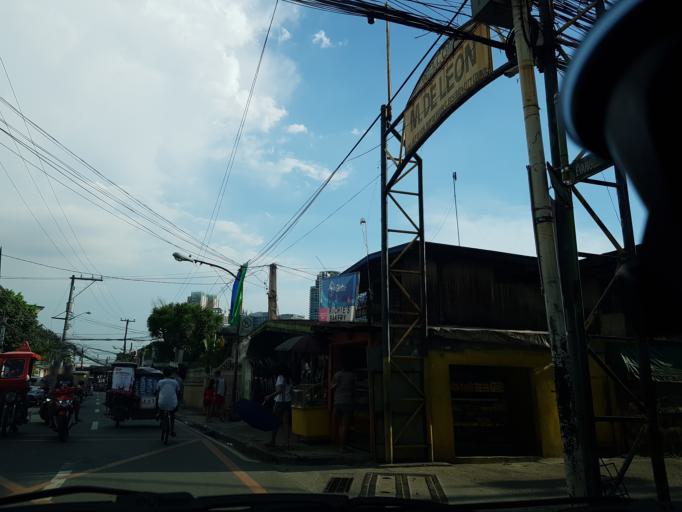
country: PH
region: Metro Manila
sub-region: Marikina
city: Calumpang
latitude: 14.6164
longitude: 121.0815
